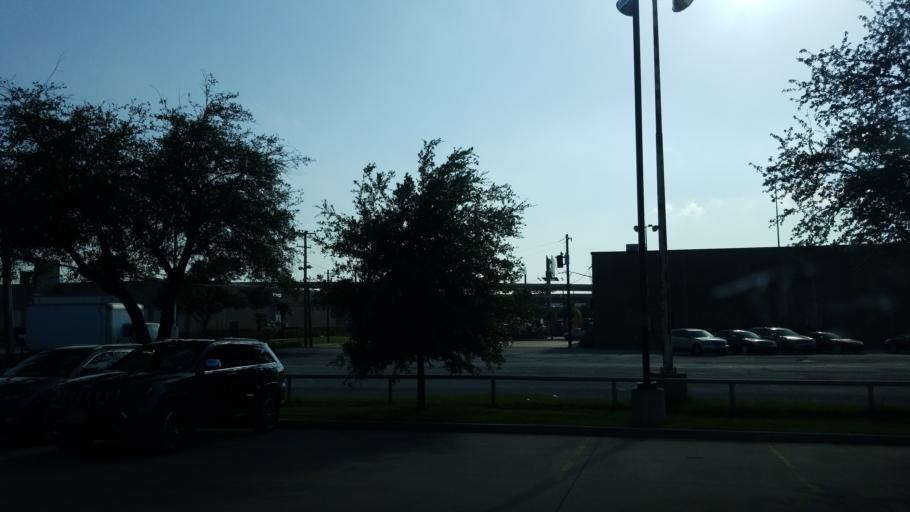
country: US
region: Texas
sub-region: Dallas County
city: Farmers Branch
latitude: 32.8742
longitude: -96.8952
